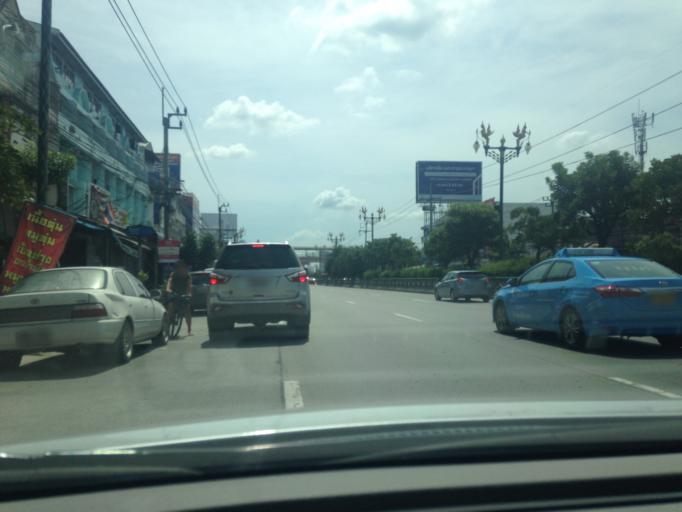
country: TH
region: Bangkok
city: Lat Krabang
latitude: 13.7012
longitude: 100.7336
